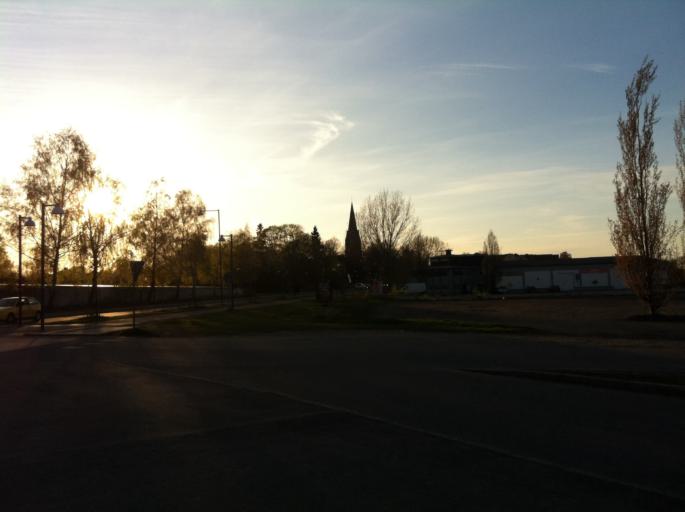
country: SE
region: OEstergoetland
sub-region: Norrkopings Kommun
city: Norrkoping
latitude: 58.5748
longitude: 16.2026
